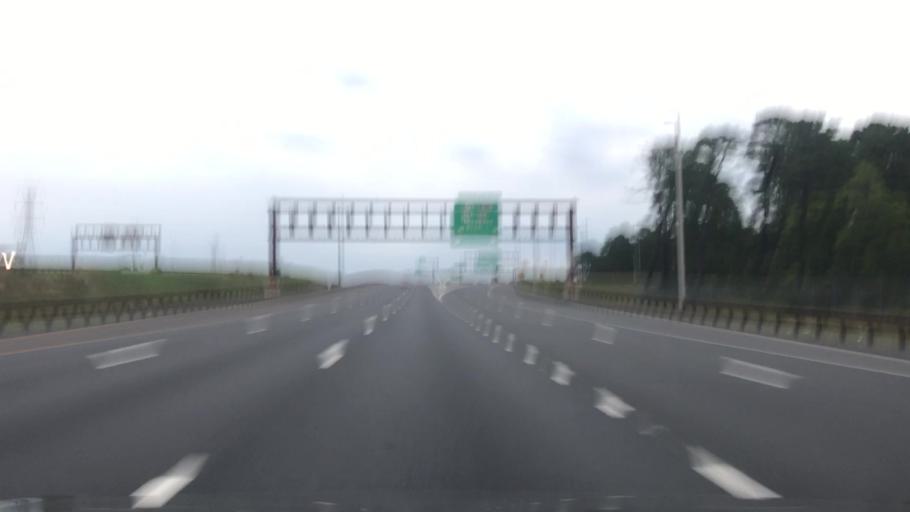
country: US
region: New Jersey
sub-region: Ocean County
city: Leisure Village
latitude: 40.0515
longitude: -74.1702
